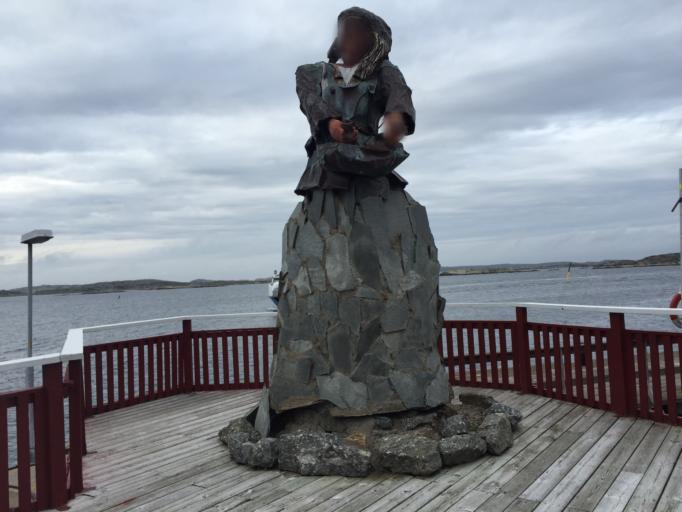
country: SE
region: Vaestra Goetaland
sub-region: Lysekils Kommun
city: Lysekil
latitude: 58.1133
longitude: 11.3668
